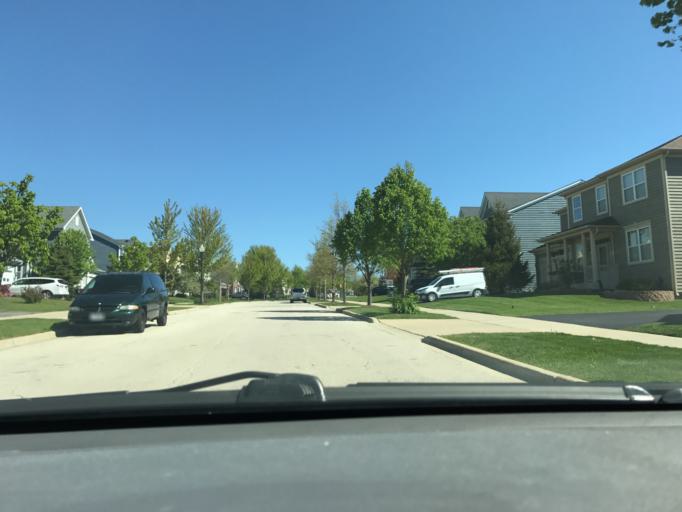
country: US
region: Illinois
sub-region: Kane County
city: Pingree Grove
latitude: 42.0301
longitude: -88.3633
